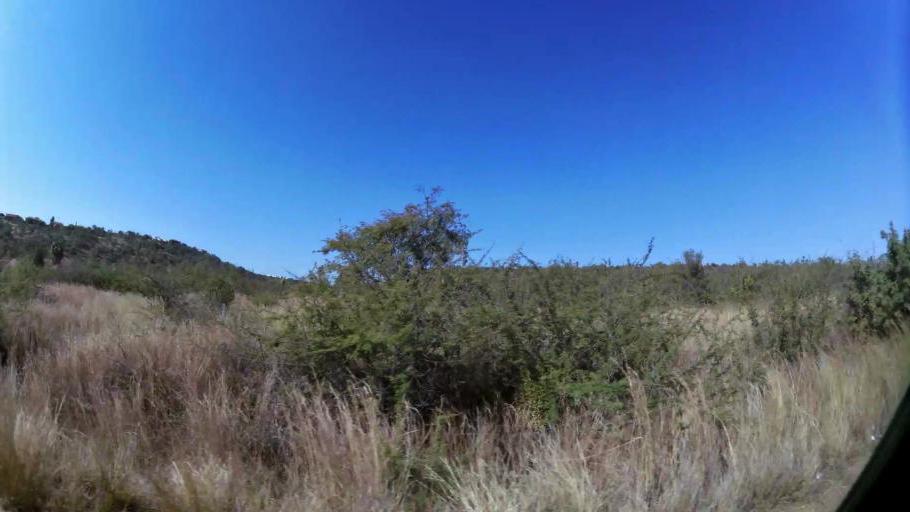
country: ZA
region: Gauteng
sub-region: City of Tshwane Metropolitan Municipality
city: Mabopane
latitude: -25.5387
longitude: 28.0818
